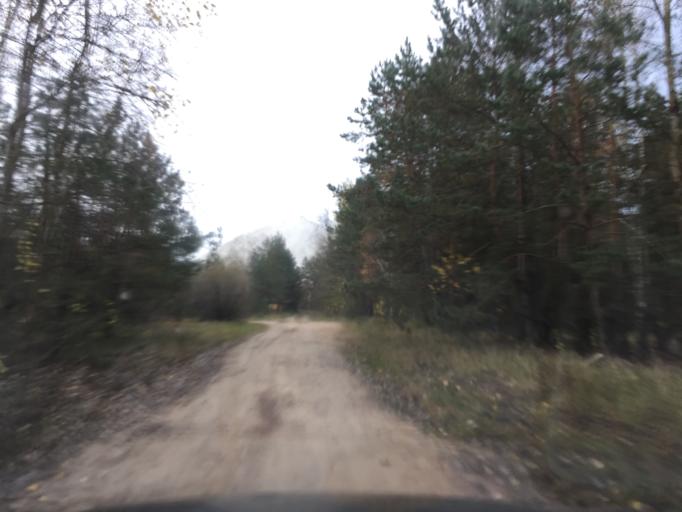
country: BY
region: Gomel
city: Kastsyukowka
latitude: 52.4334
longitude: 30.8291
